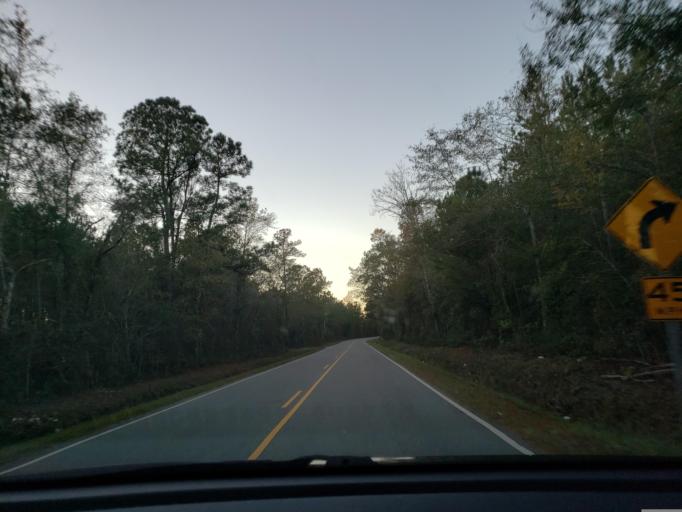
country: US
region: North Carolina
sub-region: Onslow County
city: Half Moon
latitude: 34.7203
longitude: -77.6207
